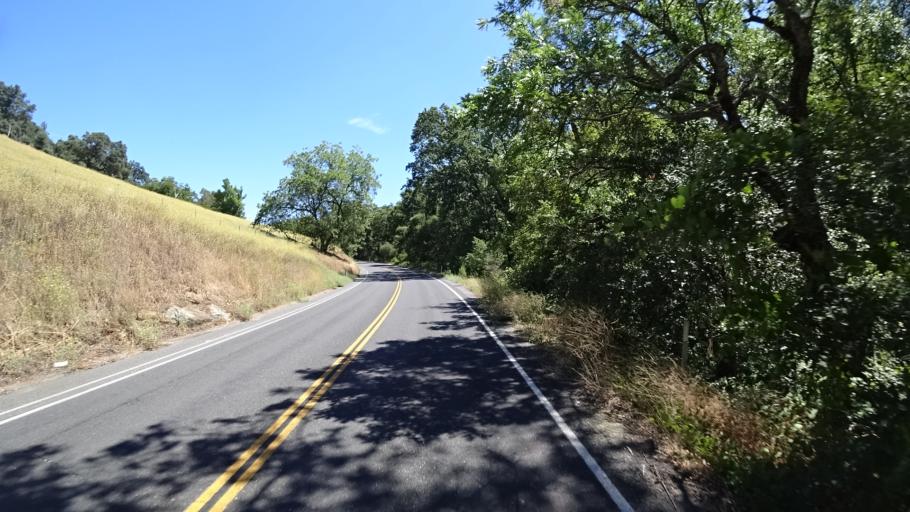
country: US
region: California
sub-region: Calaveras County
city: Murphys
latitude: 38.1120
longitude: -120.5061
